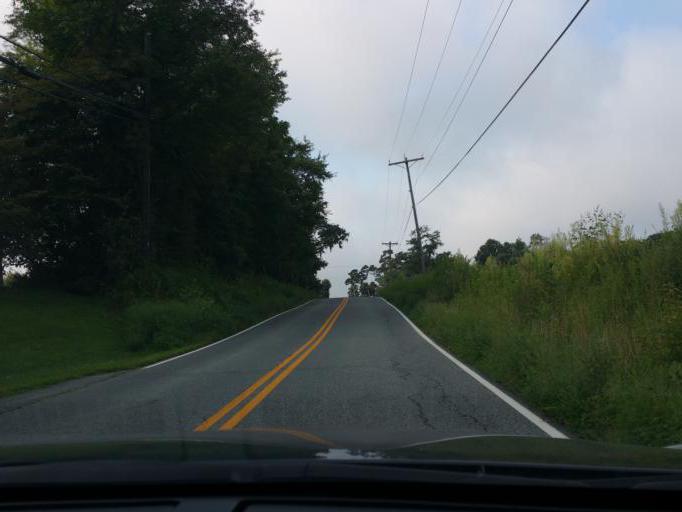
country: US
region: Maryland
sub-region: Cecil County
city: Rising Sun
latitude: 39.6359
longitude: -76.1284
